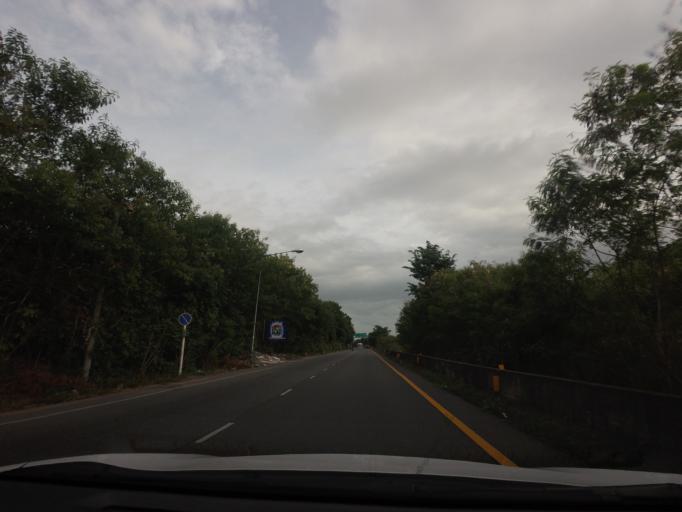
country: TH
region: Chon Buri
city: Phatthaya
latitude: 12.8968
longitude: 100.9002
